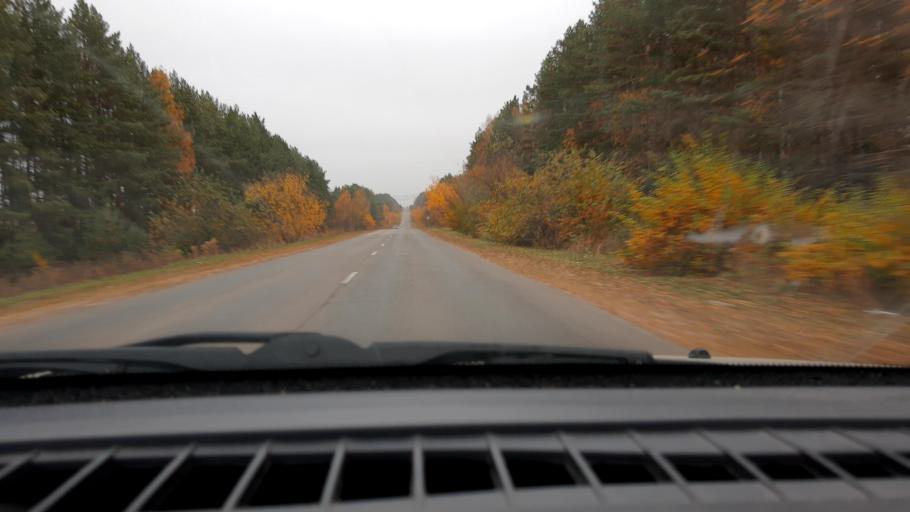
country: RU
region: Nizjnij Novgorod
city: Burevestnik
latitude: 56.0660
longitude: 43.8869
